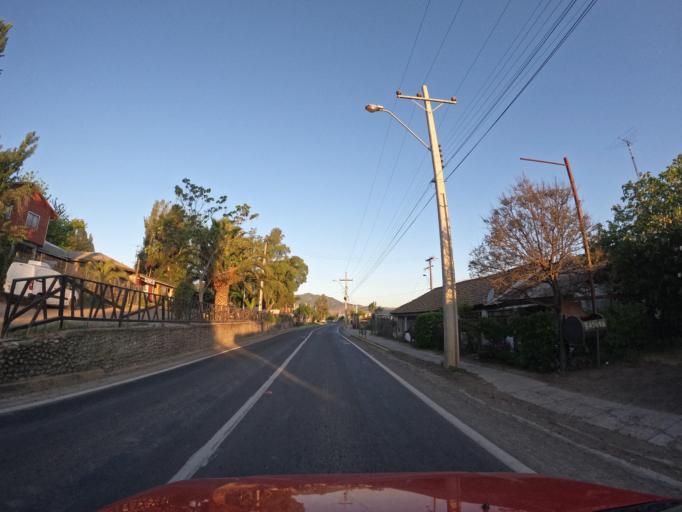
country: CL
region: Maule
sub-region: Provincia de Talca
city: Talca
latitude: -35.0894
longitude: -71.6625
